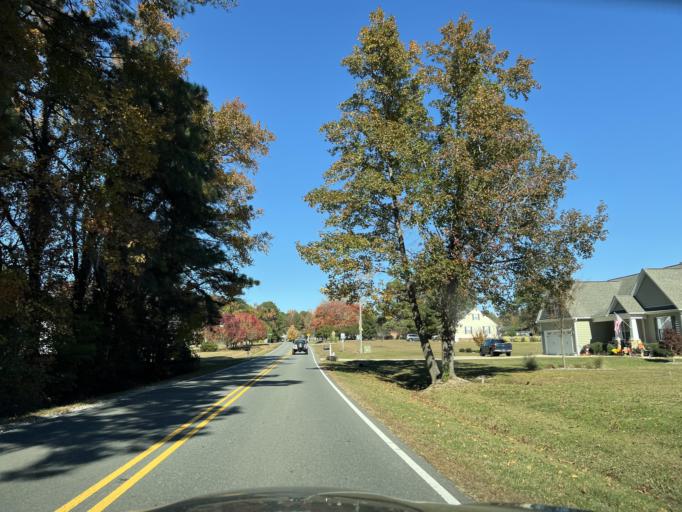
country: US
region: North Carolina
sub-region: Wake County
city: Fuquay-Varina
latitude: 35.6222
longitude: -78.7315
